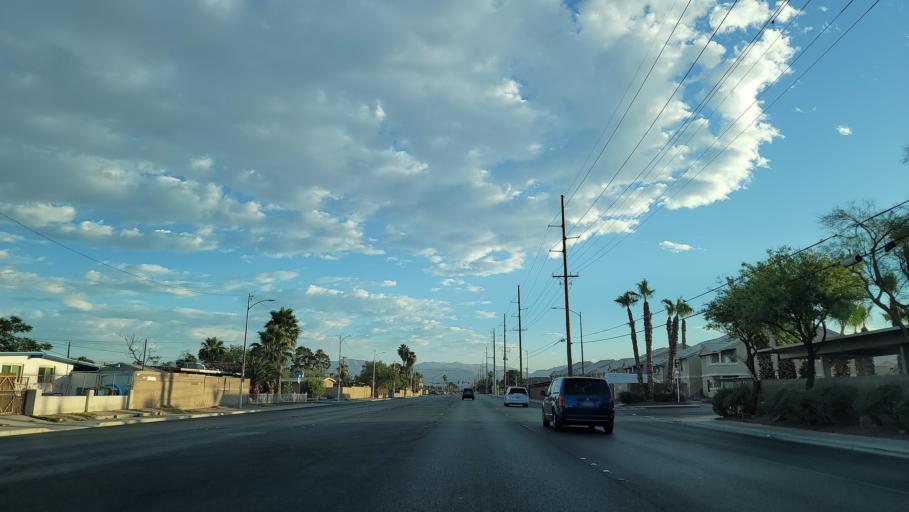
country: US
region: Nevada
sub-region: Clark County
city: North Las Vegas
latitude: 36.1921
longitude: -115.0983
